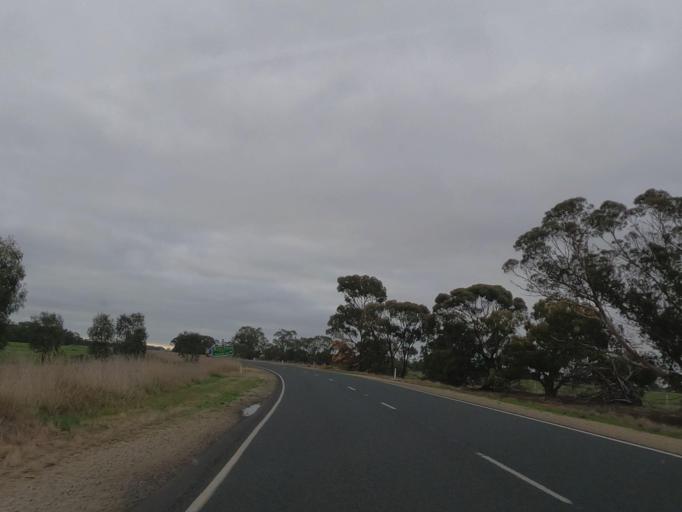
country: AU
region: Victoria
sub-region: Greater Bendigo
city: Long Gully
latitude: -36.1149
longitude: 143.9283
